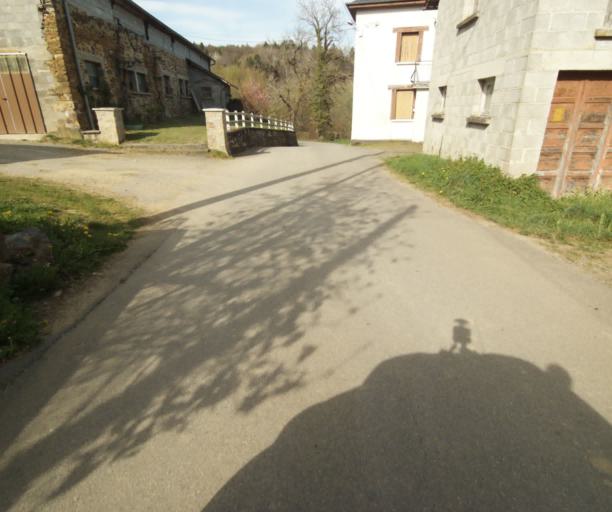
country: FR
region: Limousin
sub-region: Departement de la Correze
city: Naves
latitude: 45.3211
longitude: 1.7253
